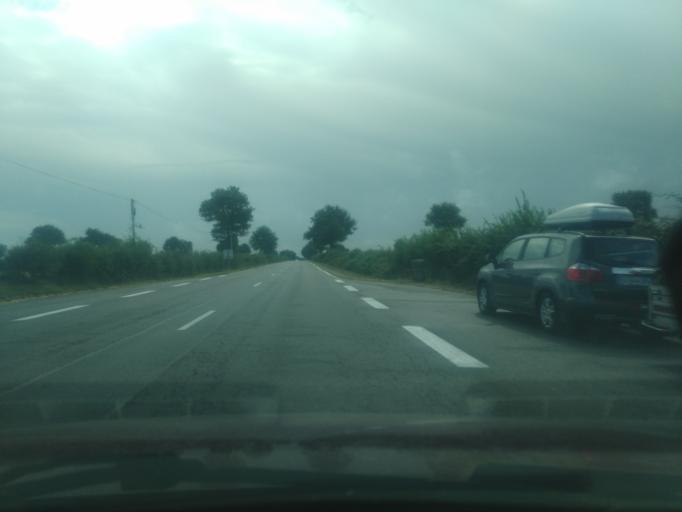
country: FR
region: Poitou-Charentes
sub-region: Departement des Deux-Sevres
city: Thenezay
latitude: 46.6574
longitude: -0.0505
